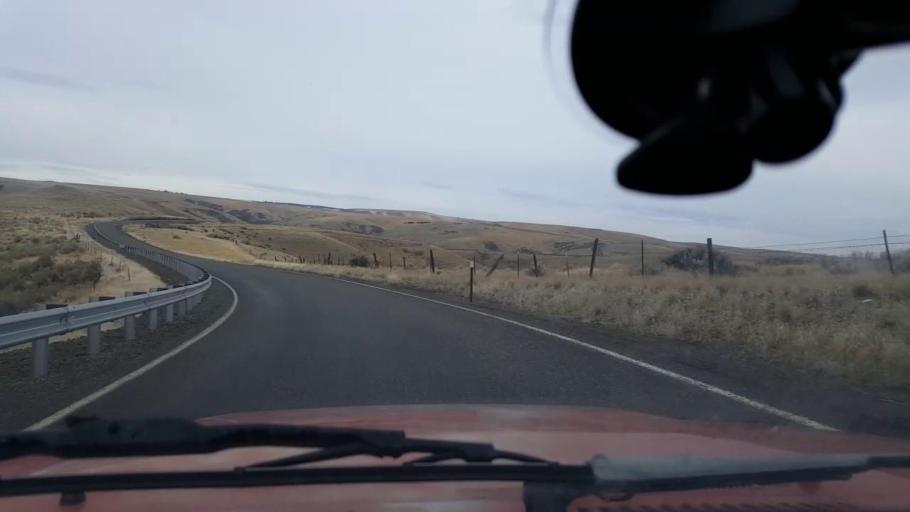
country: US
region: Washington
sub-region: Asotin County
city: Clarkston Heights-Vineland
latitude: 46.3347
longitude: -117.2872
